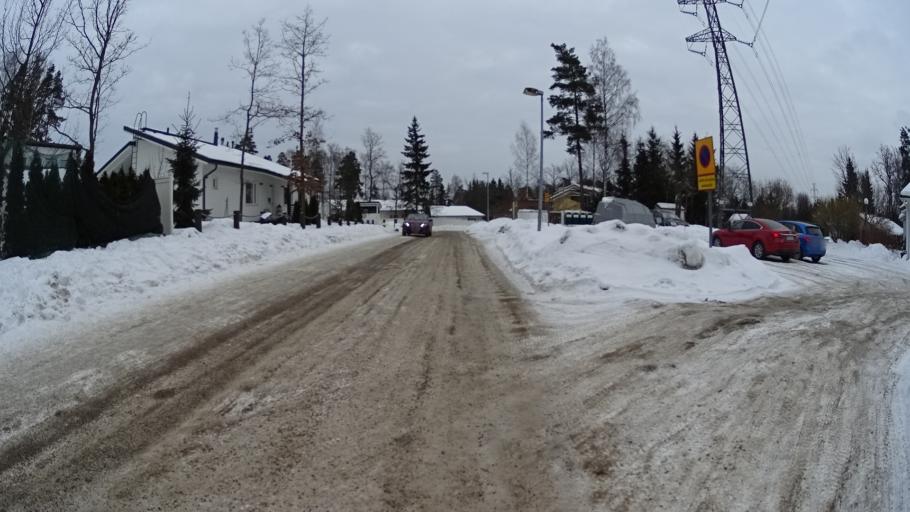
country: FI
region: Uusimaa
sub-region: Helsinki
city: Kauniainen
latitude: 60.2430
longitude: 24.7074
